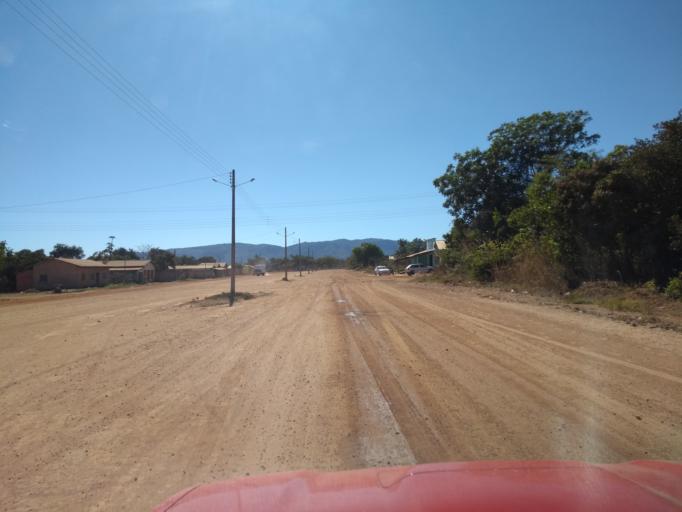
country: BR
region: Goias
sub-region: Cavalcante
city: Cavalcante
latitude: -13.7986
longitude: -47.4437
